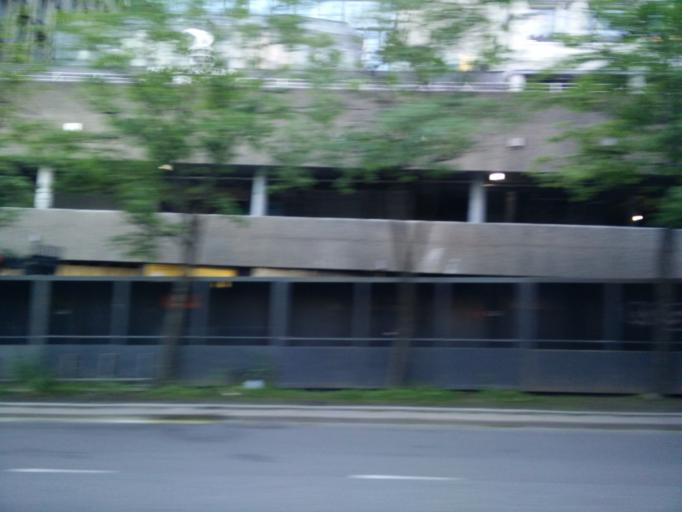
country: NO
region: Oslo
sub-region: Oslo
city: Oslo
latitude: 59.9131
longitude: 10.7288
